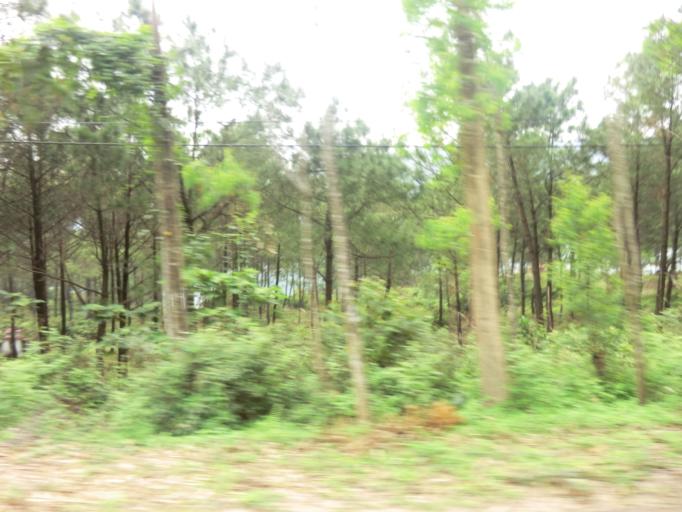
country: VN
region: Quang Binh
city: Ba Don
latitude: 17.6980
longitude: 106.4363
